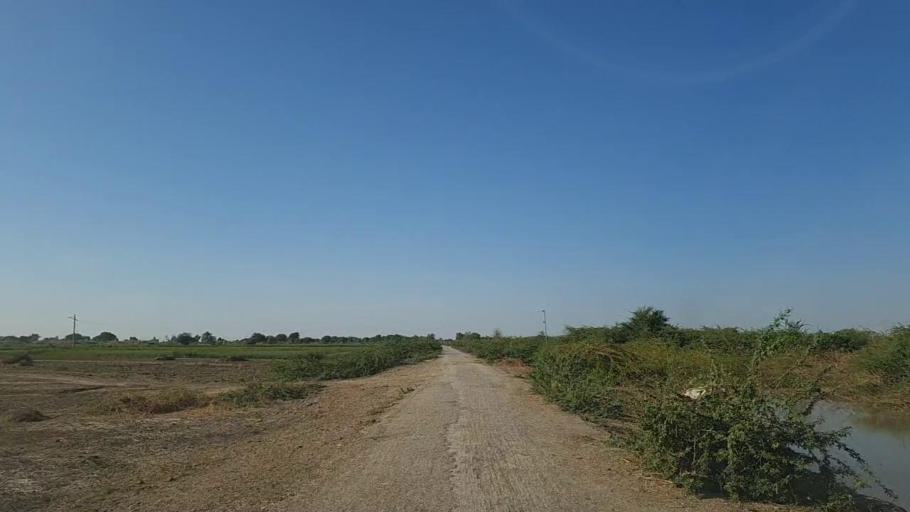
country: PK
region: Sindh
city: Samaro
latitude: 25.2575
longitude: 69.4900
